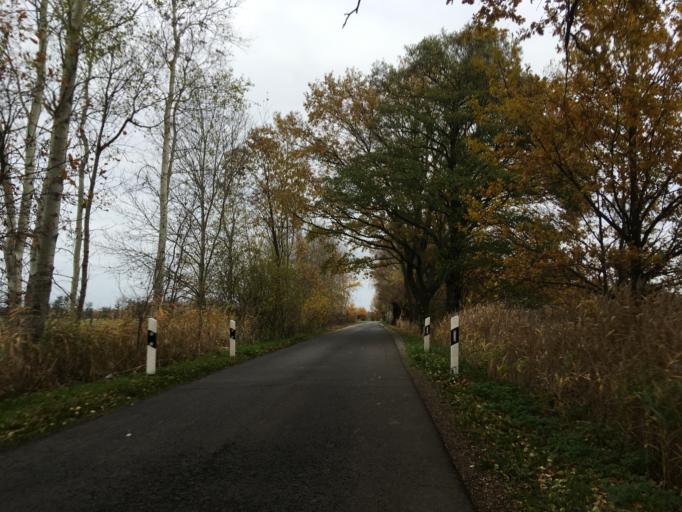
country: DE
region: Brandenburg
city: Drehnow
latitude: 51.8562
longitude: 14.3388
